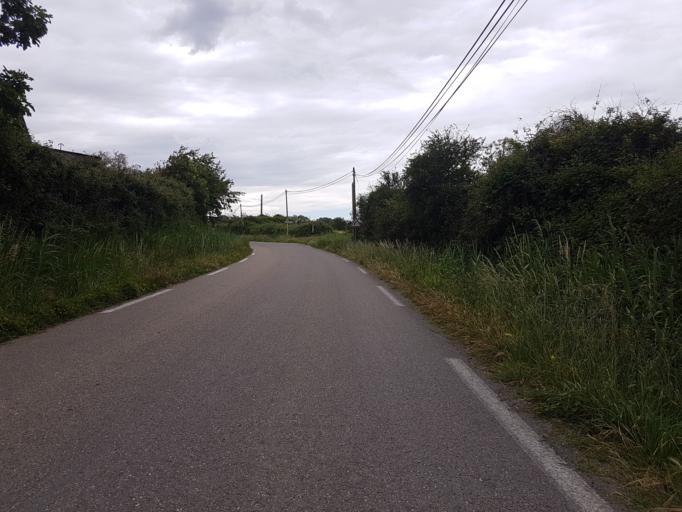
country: FR
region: Languedoc-Roussillon
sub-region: Departement du Gard
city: Saint-Gilles
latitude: 43.6704
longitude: 4.4387
